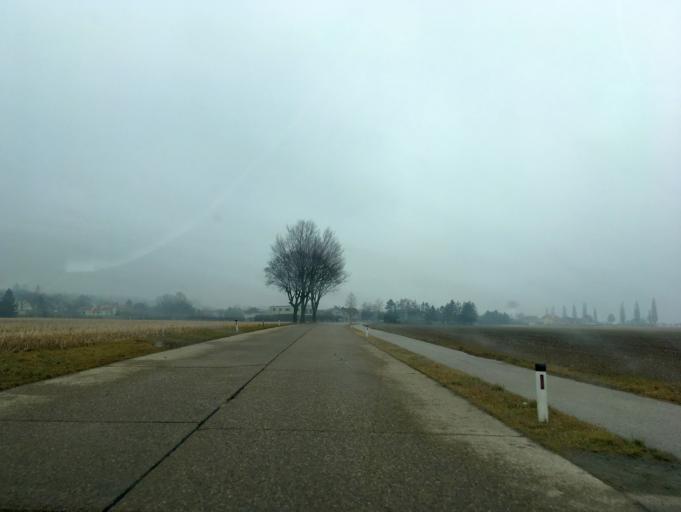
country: AT
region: Lower Austria
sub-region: Politischer Bezirk Bruck an der Leitha
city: Trautmannsdorf an der Leitha
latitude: 48.0457
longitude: 16.6655
